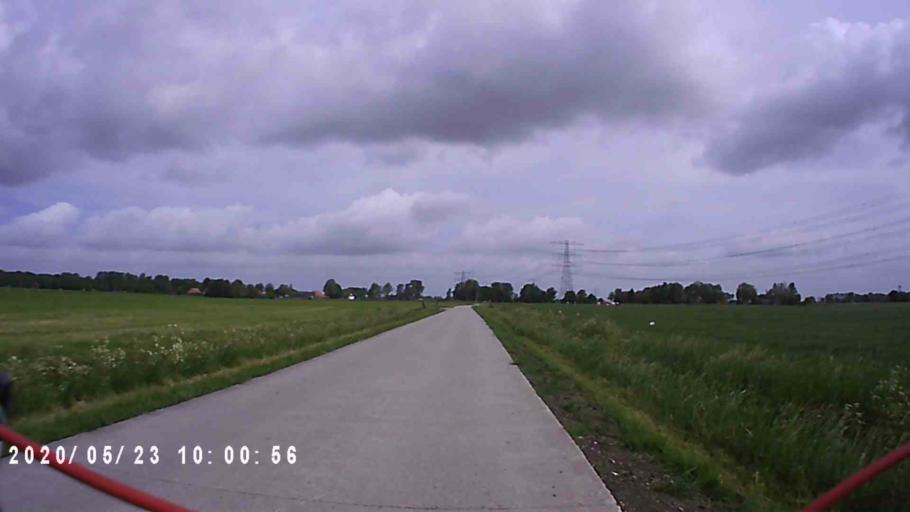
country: NL
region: Groningen
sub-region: Gemeente Appingedam
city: Appingedam
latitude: 53.3138
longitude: 6.8202
